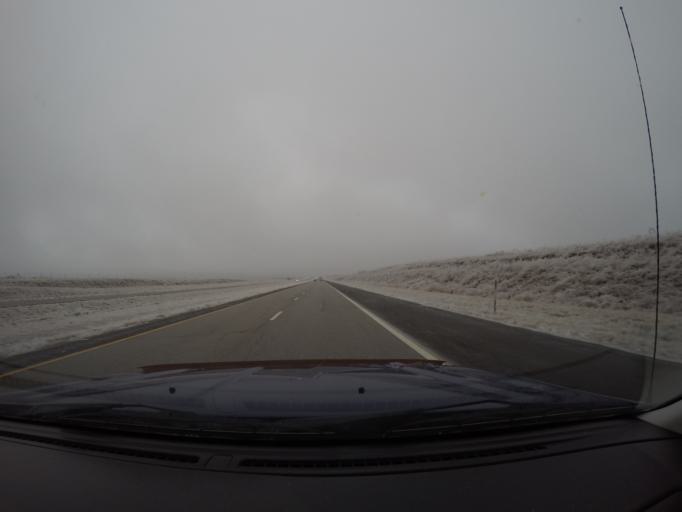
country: US
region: Kansas
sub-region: Riley County
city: Manhattan
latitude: 39.1055
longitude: -96.5381
